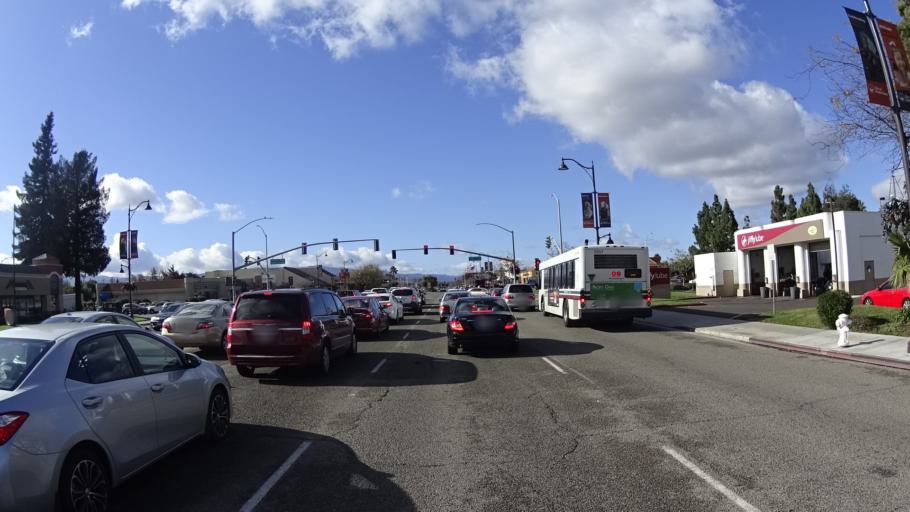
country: US
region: California
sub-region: Santa Clara County
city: Santa Clara
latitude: 37.3524
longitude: -121.9769
